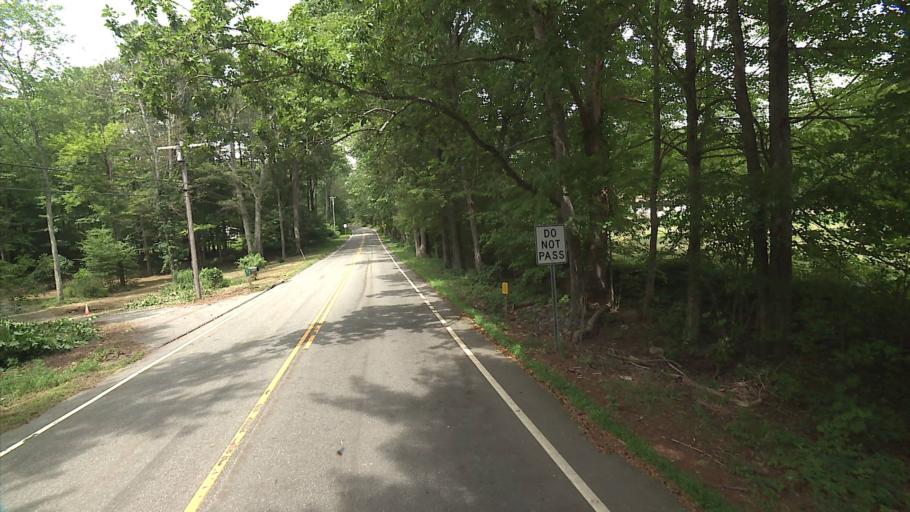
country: US
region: Massachusetts
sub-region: Hampden County
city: Holland
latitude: 41.9577
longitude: -72.1051
